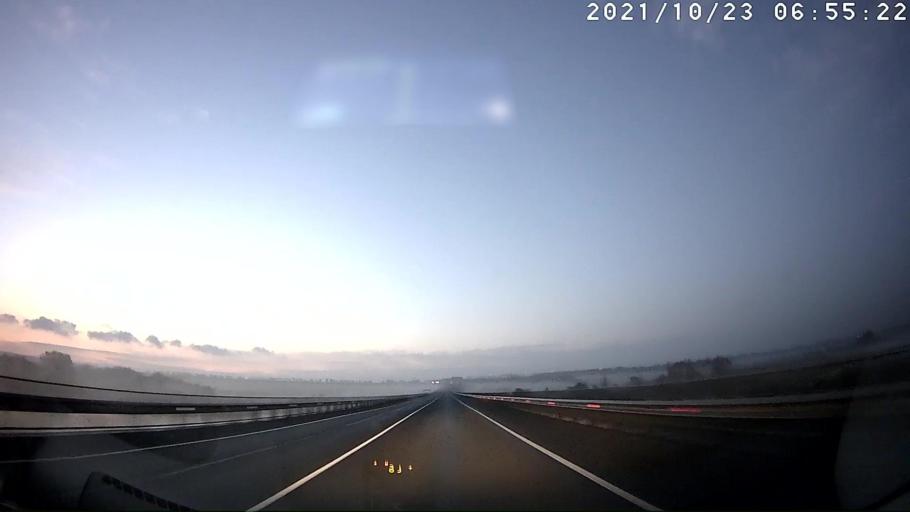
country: RU
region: Saratov
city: Dukhovnitskoye
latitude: 52.7382
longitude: 48.2550
